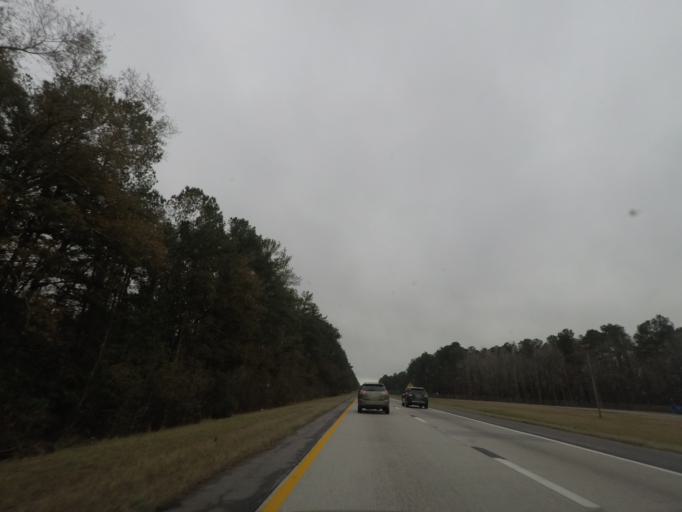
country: US
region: South Carolina
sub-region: Dorchester County
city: Saint George
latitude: 33.1593
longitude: -80.6215
